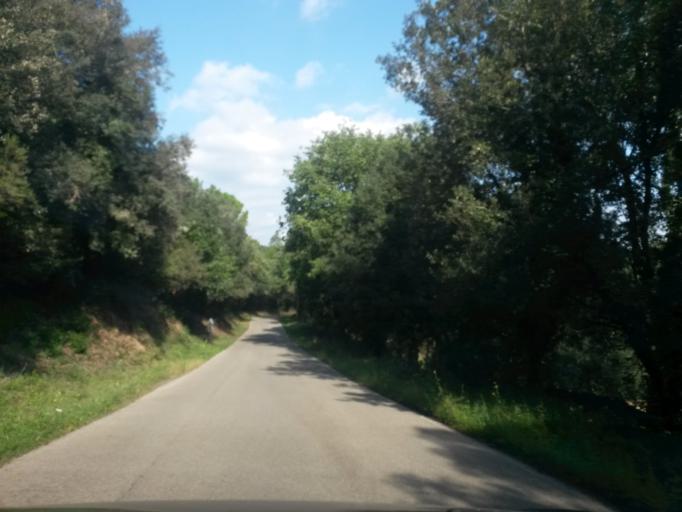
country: ES
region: Catalonia
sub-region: Provincia de Girona
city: Bescano
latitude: 41.9570
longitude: 2.7324
